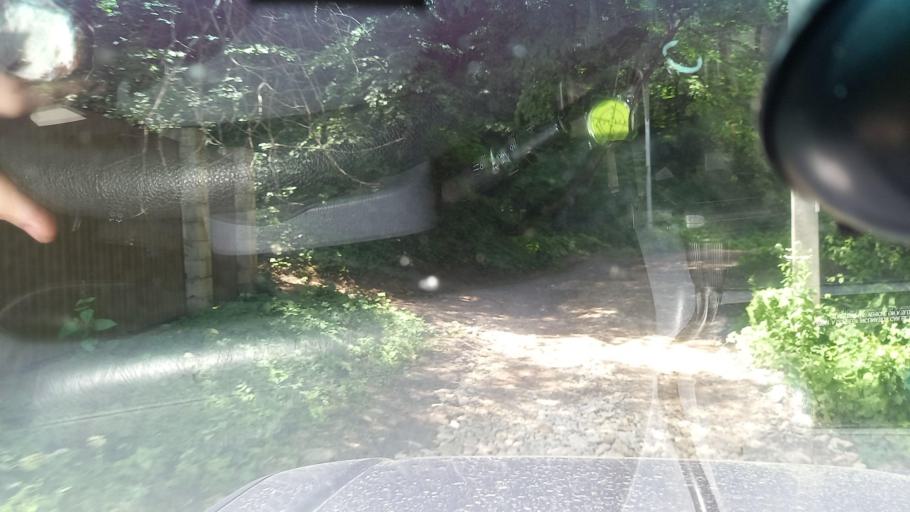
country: RU
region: Adygeya
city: Kamennomostskiy
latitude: 44.2934
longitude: 40.1619
